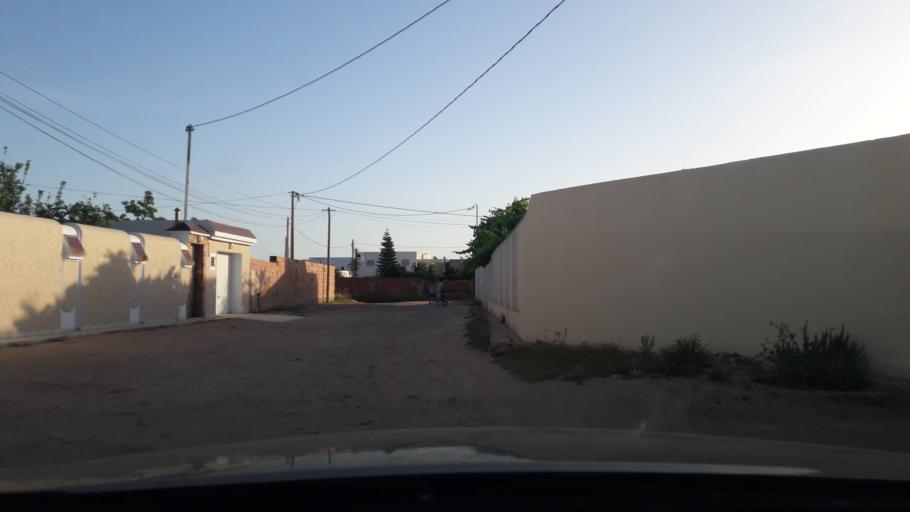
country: TN
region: Safaqis
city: Al Qarmadah
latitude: 34.7930
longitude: 10.7538
